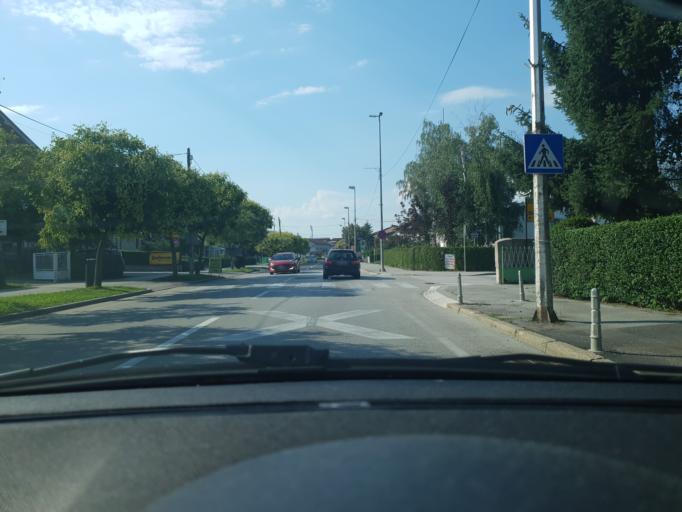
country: HR
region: Zagrebacka
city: Zapresic
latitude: 45.8588
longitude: 15.8047
